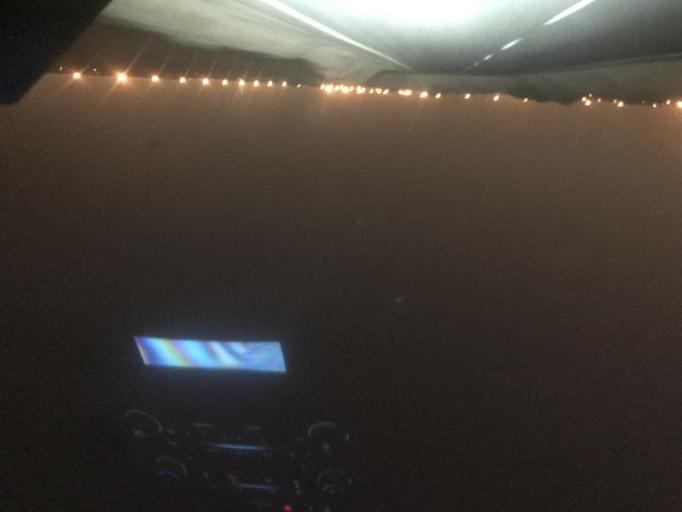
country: SA
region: Ar Riyad
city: Riyadh
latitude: 24.7625
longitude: 46.5864
